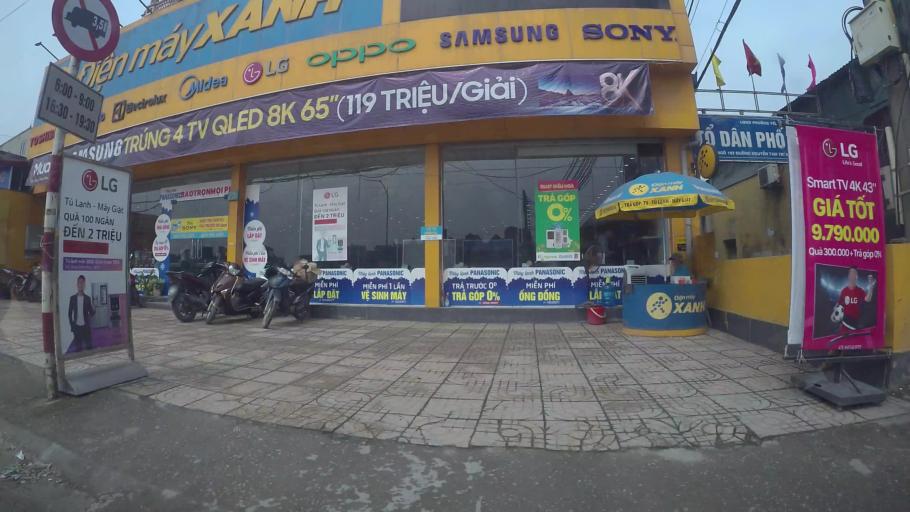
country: VN
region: Ha Noi
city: Van Dien
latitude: 20.9668
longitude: 105.8679
